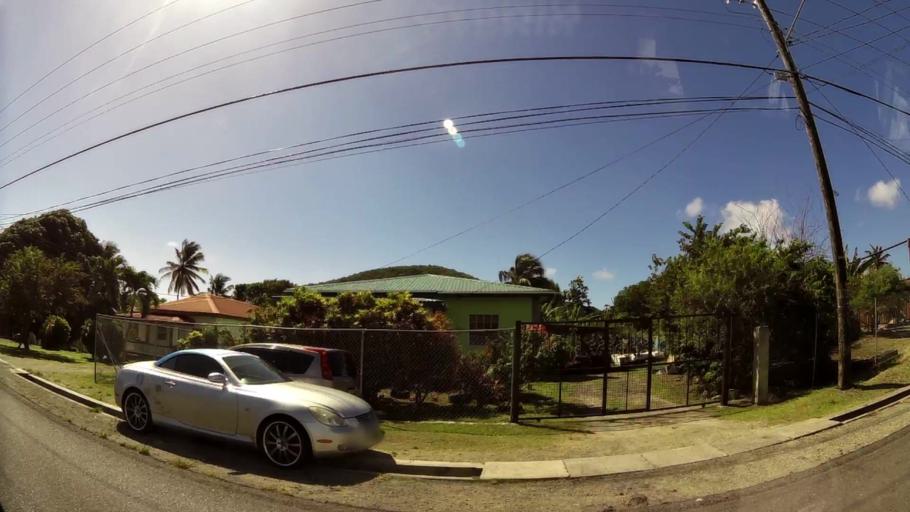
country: LC
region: Laborie Quarter
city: Laborie
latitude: 13.7484
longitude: -60.9630
